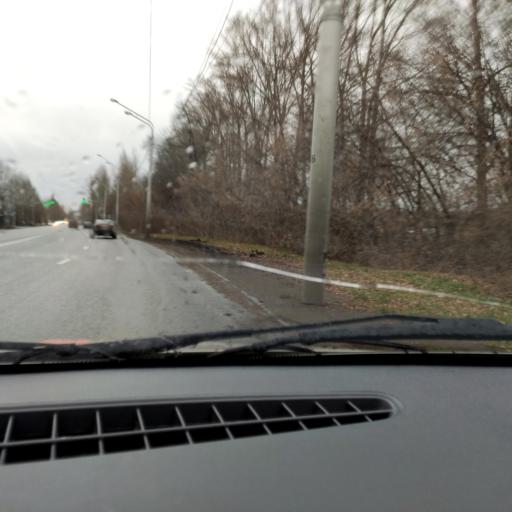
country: RU
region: Bashkortostan
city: Avdon
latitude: 54.6911
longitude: 55.8182
